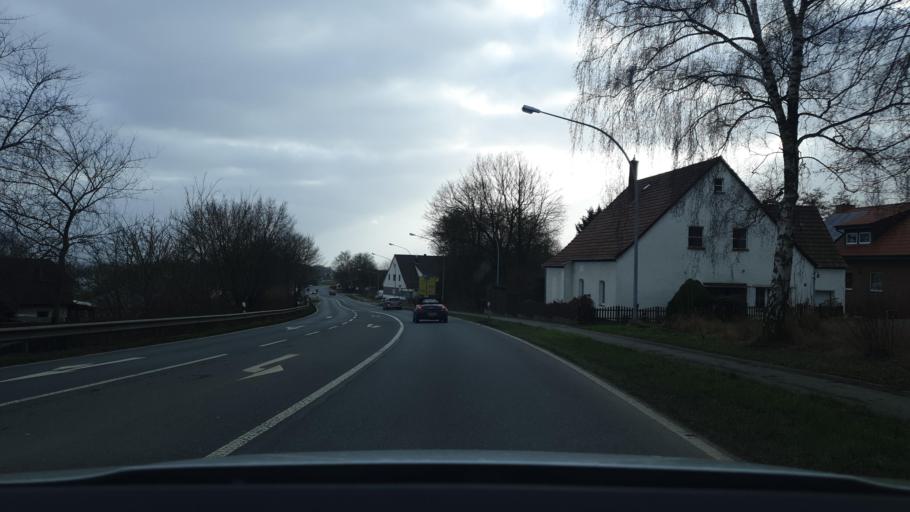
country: DE
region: North Rhine-Westphalia
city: Lubbecke
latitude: 52.2807
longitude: 8.6330
